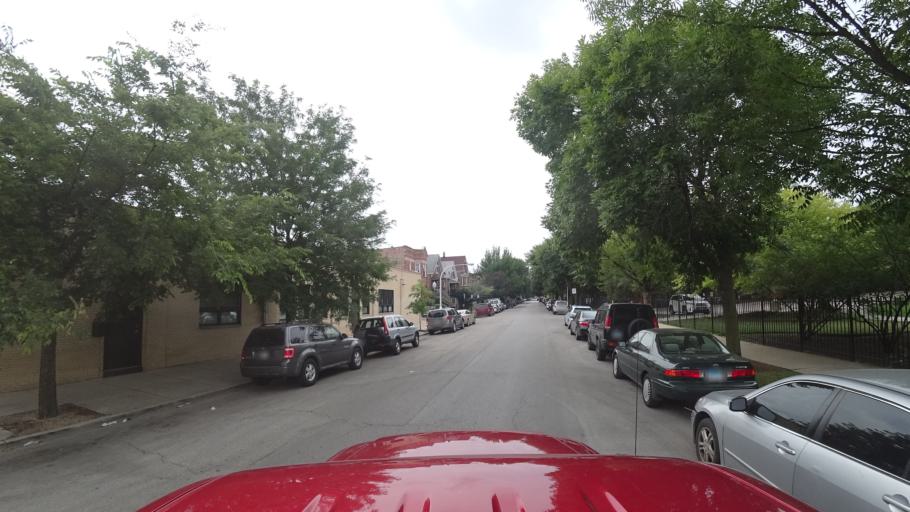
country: US
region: Illinois
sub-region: Cook County
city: Chicago
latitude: 41.8303
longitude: -87.6730
